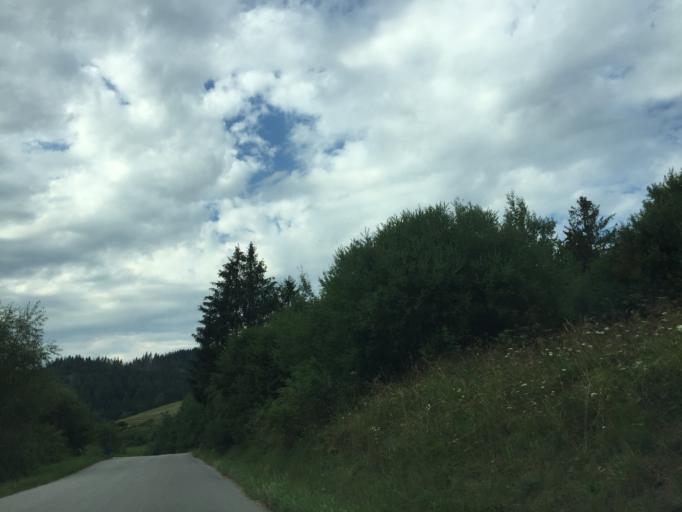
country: SK
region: Zilinsky
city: Namestovo
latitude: 49.3858
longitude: 19.3551
